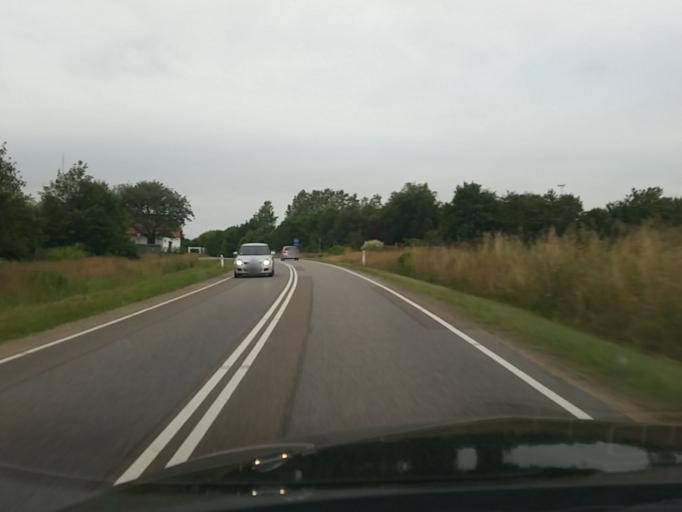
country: DK
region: South Denmark
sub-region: Billund Kommune
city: Grindsted
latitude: 55.6564
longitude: 8.8069
